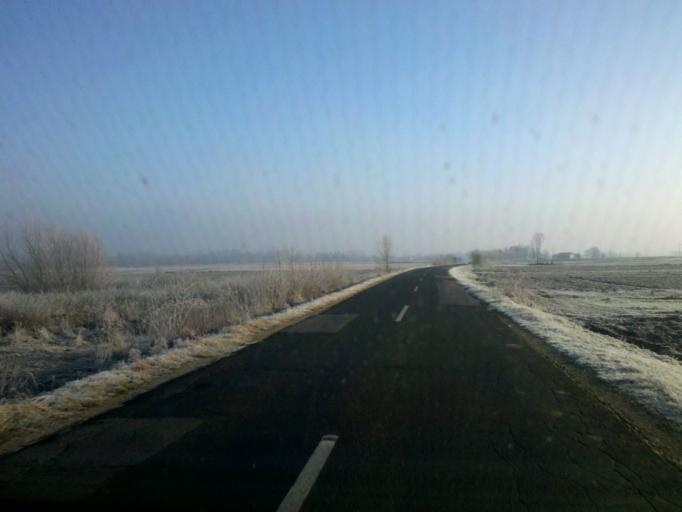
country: HR
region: Medimurska
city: Kotoriba
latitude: 46.2873
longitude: 16.7614
